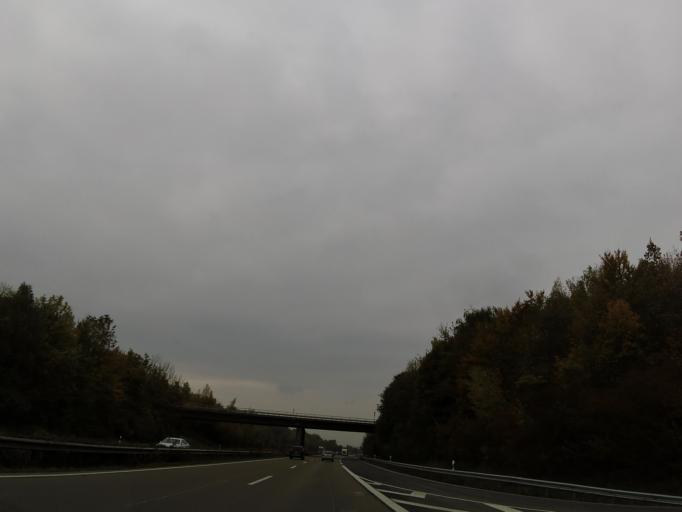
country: DE
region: Rheinland-Pfalz
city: Spiesheim
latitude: 49.7944
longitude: 8.1405
